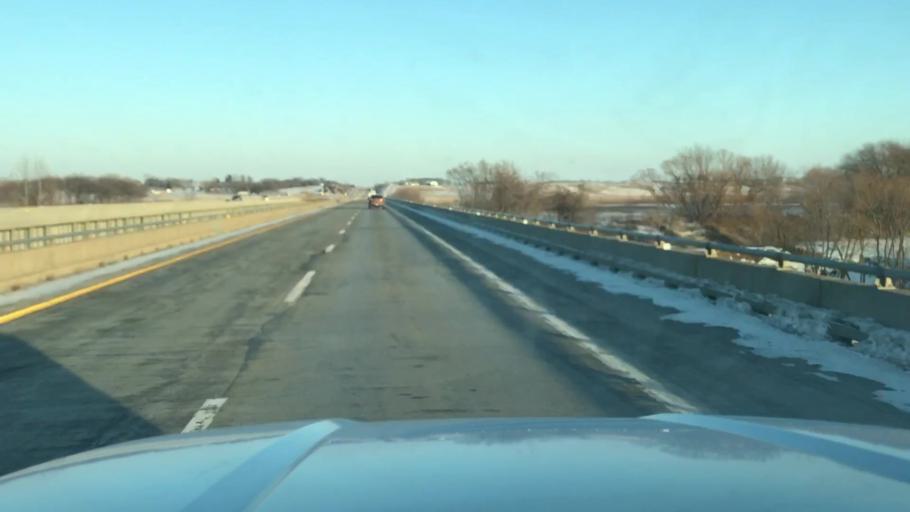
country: US
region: Missouri
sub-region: Buchanan County
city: Saint Joseph
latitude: 39.7478
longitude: -94.7276
